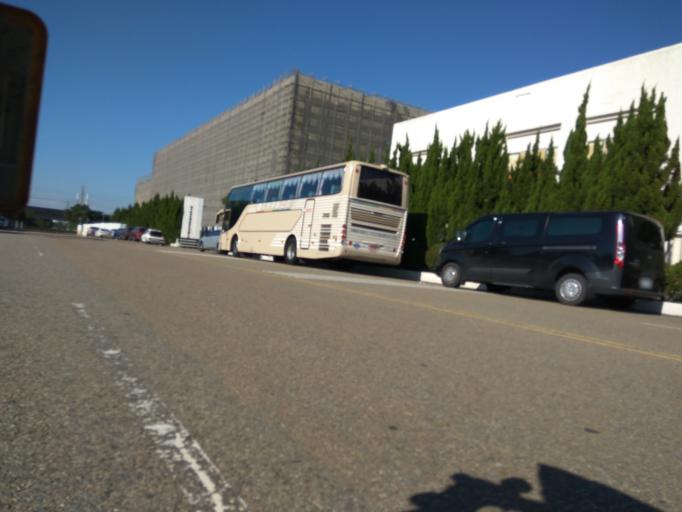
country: TW
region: Taiwan
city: Taoyuan City
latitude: 24.9711
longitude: 121.1768
